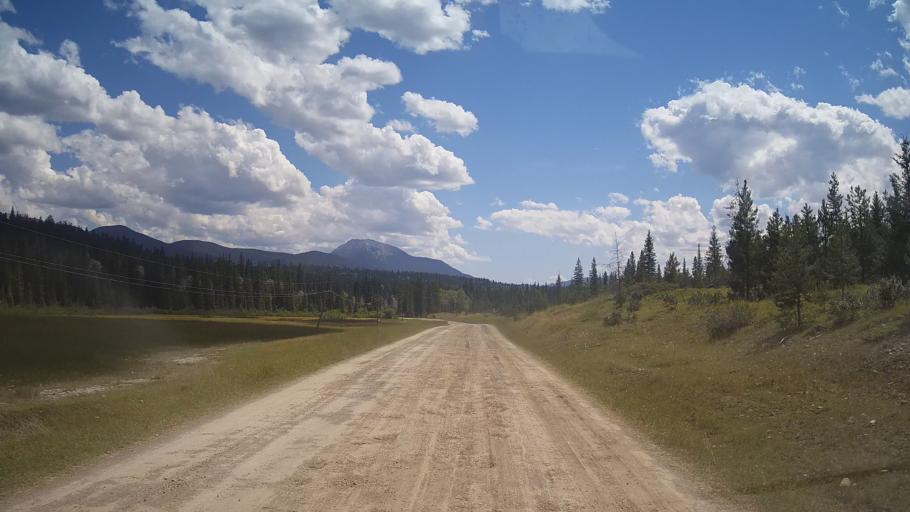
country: CA
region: British Columbia
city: Lillooet
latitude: 51.2962
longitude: -121.9812
